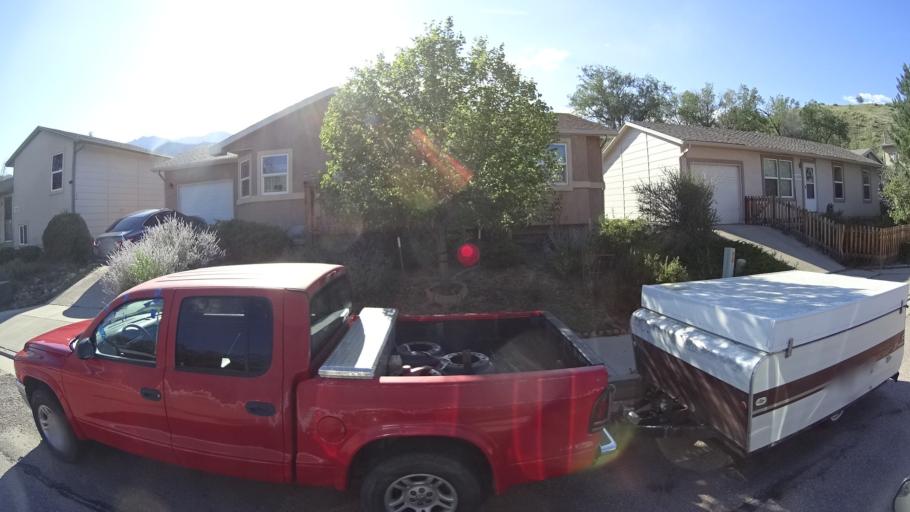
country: US
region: Colorado
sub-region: El Paso County
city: Manitou Springs
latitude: 38.8380
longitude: -104.8723
